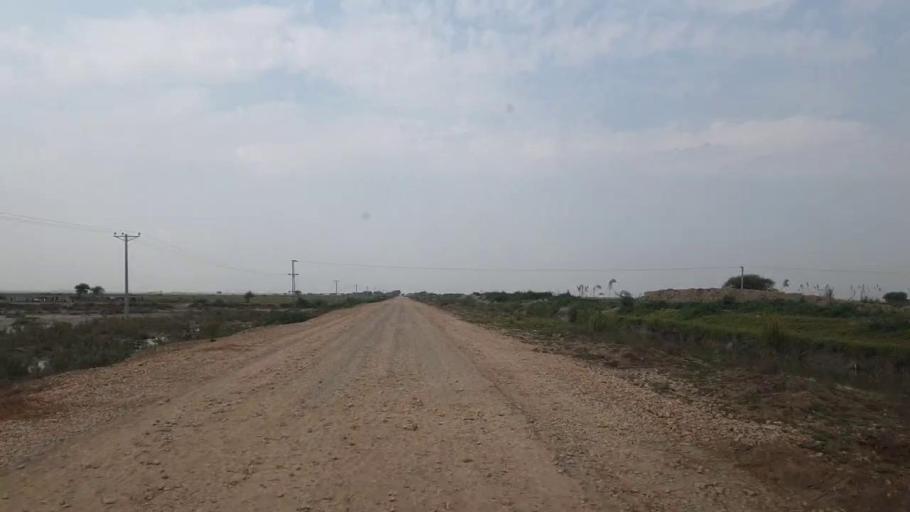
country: PK
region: Sindh
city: Kario
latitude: 24.6157
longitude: 68.5872
